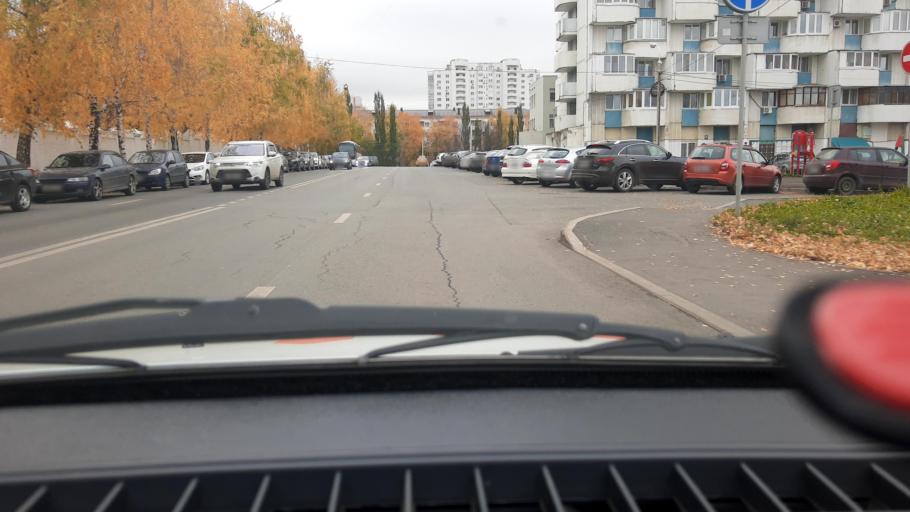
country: RU
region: Bashkortostan
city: Ufa
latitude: 54.7649
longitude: 56.0131
